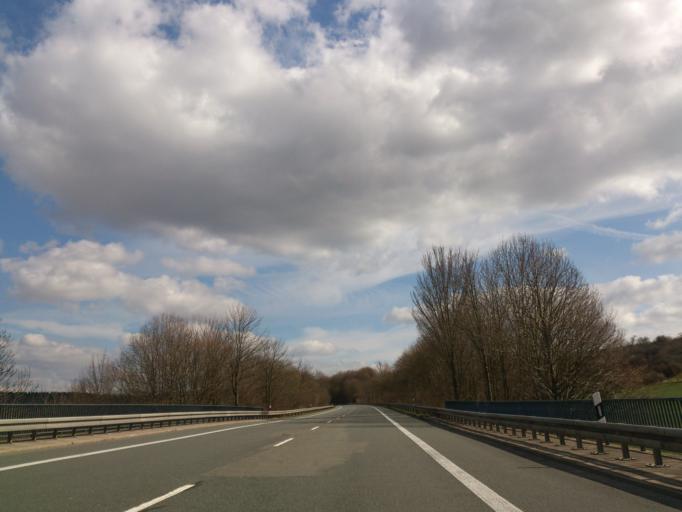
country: DE
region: North Rhine-Westphalia
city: Brakel
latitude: 51.7004
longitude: 9.1470
